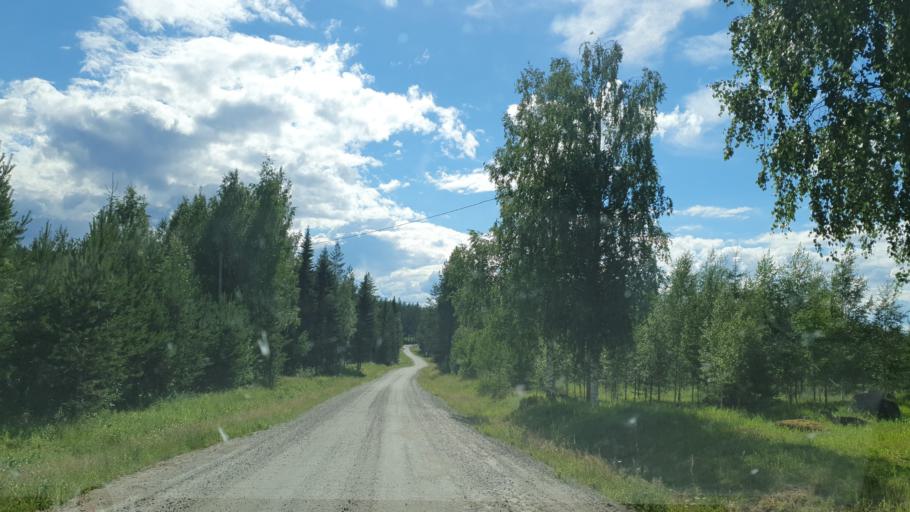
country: FI
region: Kainuu
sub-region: Kehys-Kainuu
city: Kuhmo
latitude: 64.1477
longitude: 29.7836
